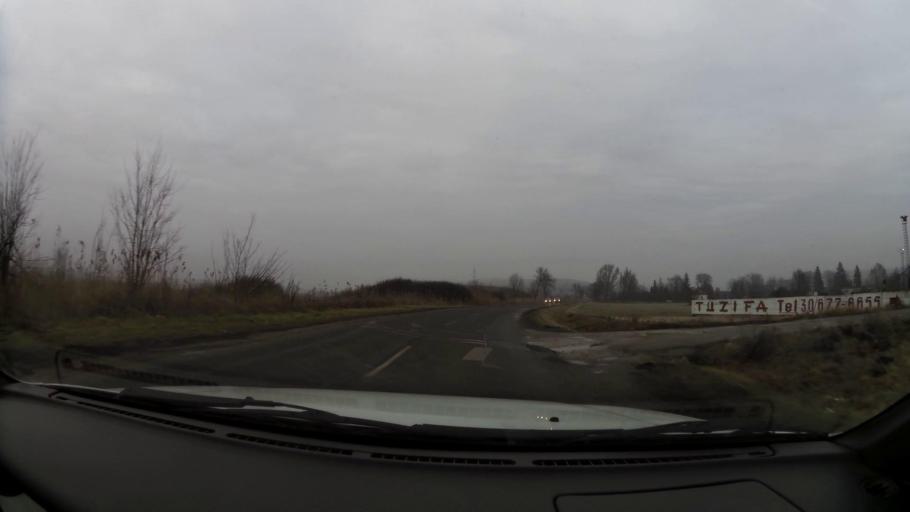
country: HU
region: Borsod-Abauj-Zemplen
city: Izsofalva
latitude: 48.2871
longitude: 20.6581
